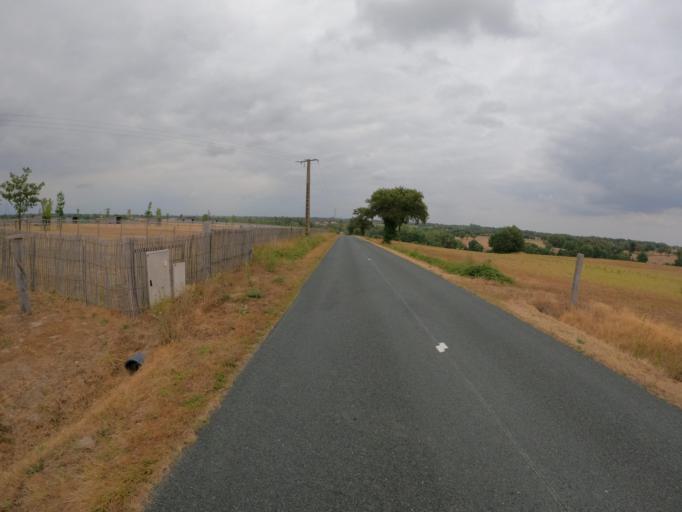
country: FR
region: Pays de la Loire
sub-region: Departement de la Vendee
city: Les Landes-Genusson
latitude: 46.9870
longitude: -1.1103
